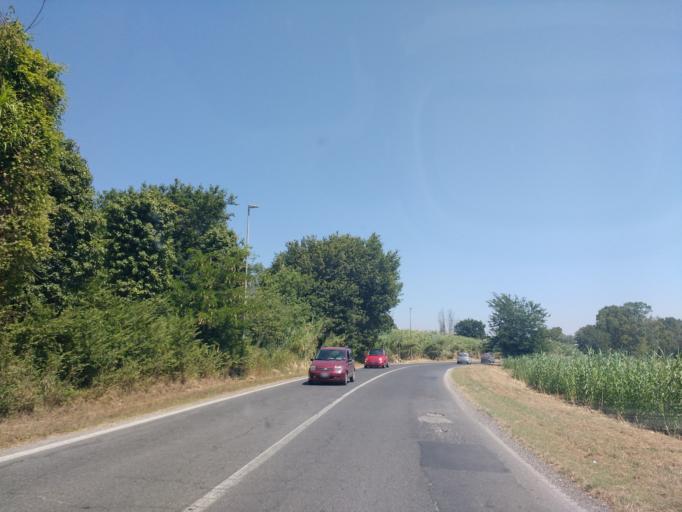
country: IT
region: Latium
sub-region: Citta metropolitana di Roma Capitale
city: Maccarese
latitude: 41.8733
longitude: 12.2093
